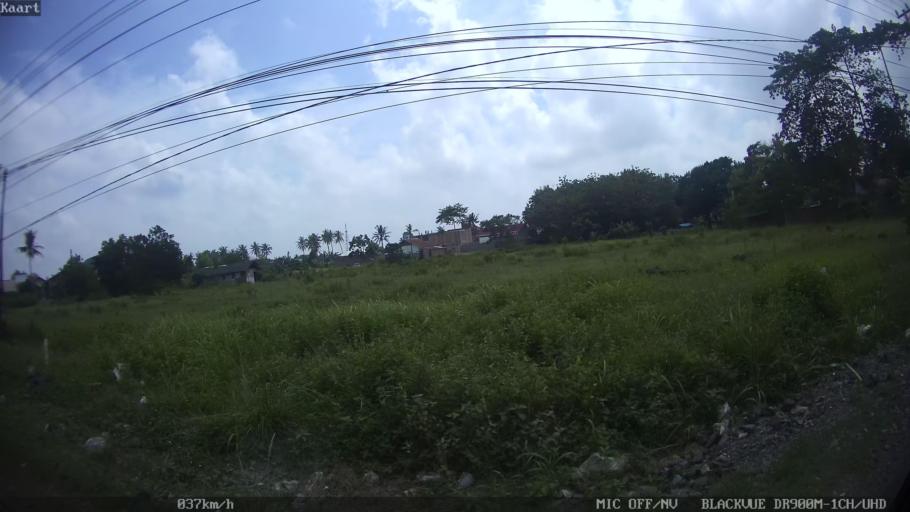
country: ID
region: Lampung
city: Kedaton
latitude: -5.3582
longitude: 105.3020
